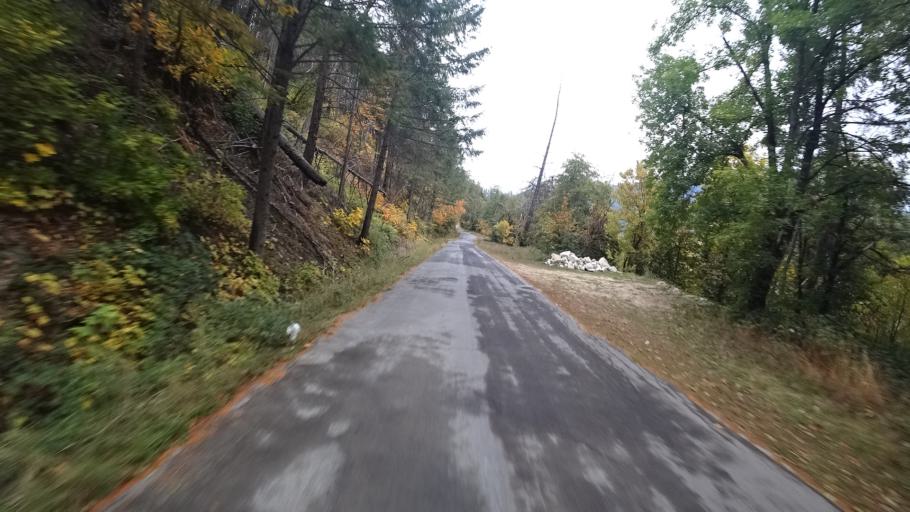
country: US
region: California
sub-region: Siskiyou County
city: Happy Camp
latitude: 41.8276
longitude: -123.1918
